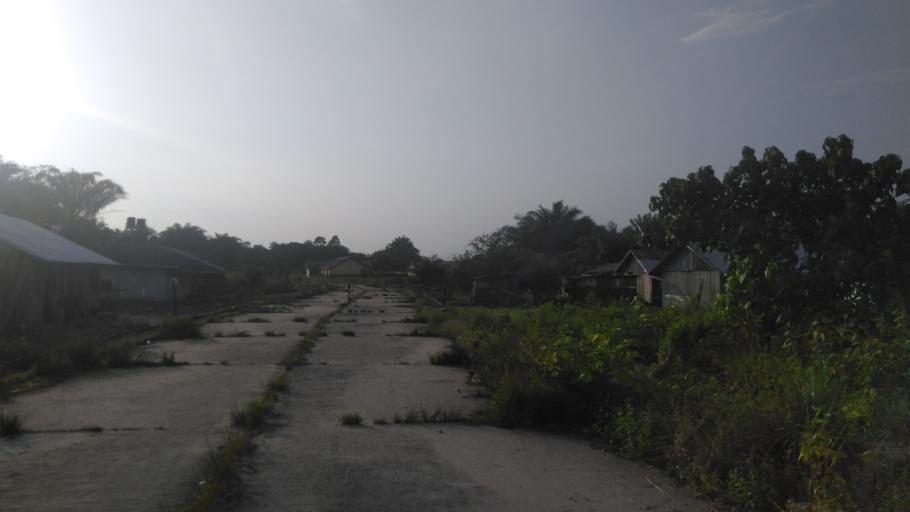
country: NG
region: Delta
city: Sapele
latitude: 5.8401
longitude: 5.1219
